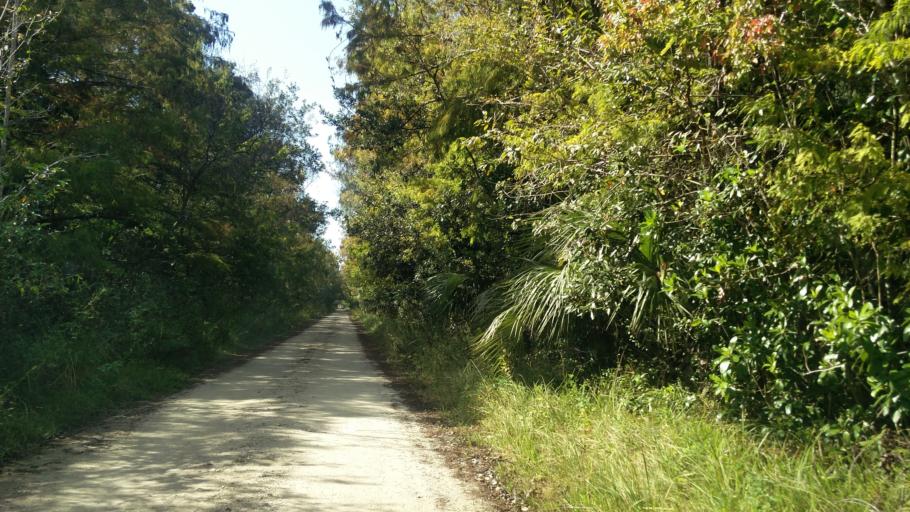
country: US
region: Florida
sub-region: Collier County
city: Lely Resort
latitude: 25.9800
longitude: -81.3915
